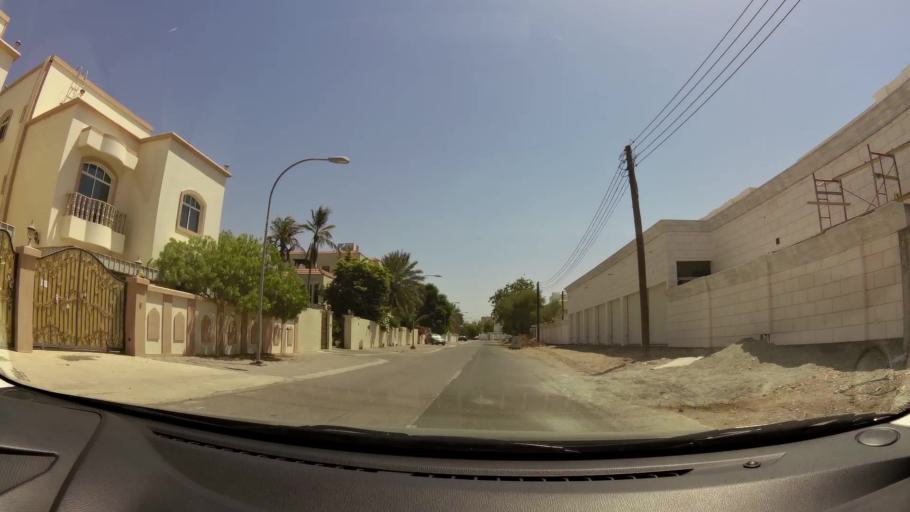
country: OM
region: Muhafazat Masqat
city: As Sib al Jadidah
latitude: 23.6299
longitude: 58.2260
